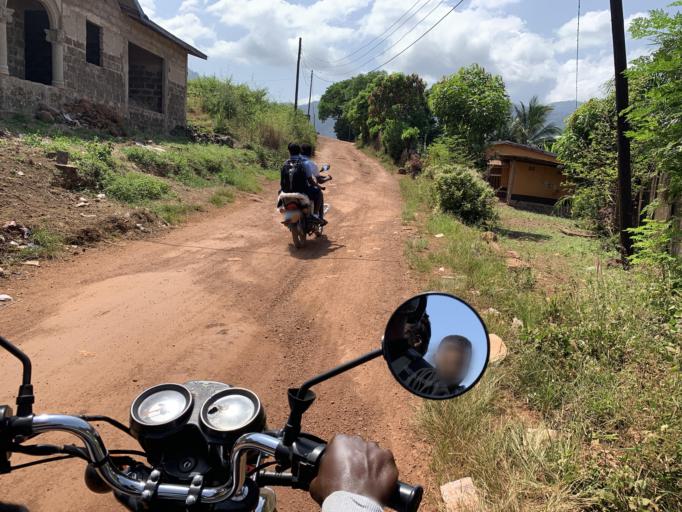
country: SL
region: Western Area
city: Hastings
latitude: 8.3821
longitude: -13.1444
